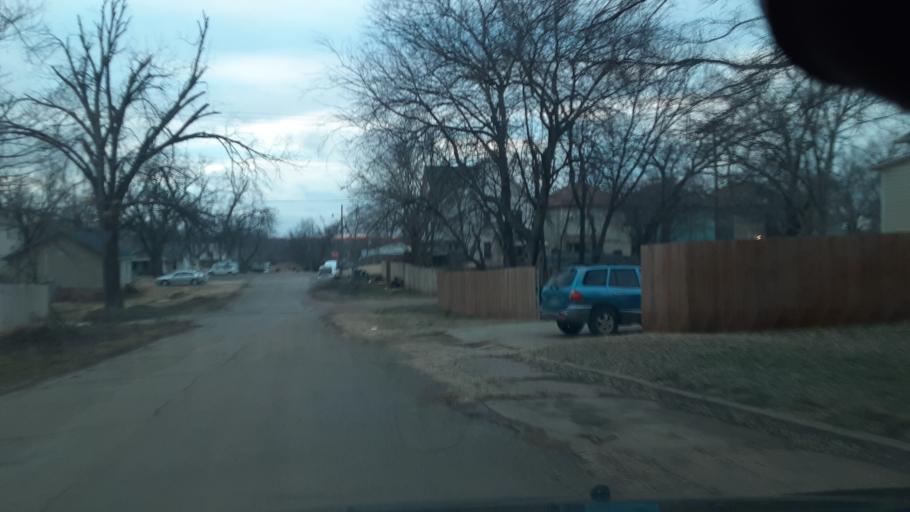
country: US
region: Oklahoma
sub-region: Logan County
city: Guthrie
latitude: 35.8833
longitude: -97.4230
